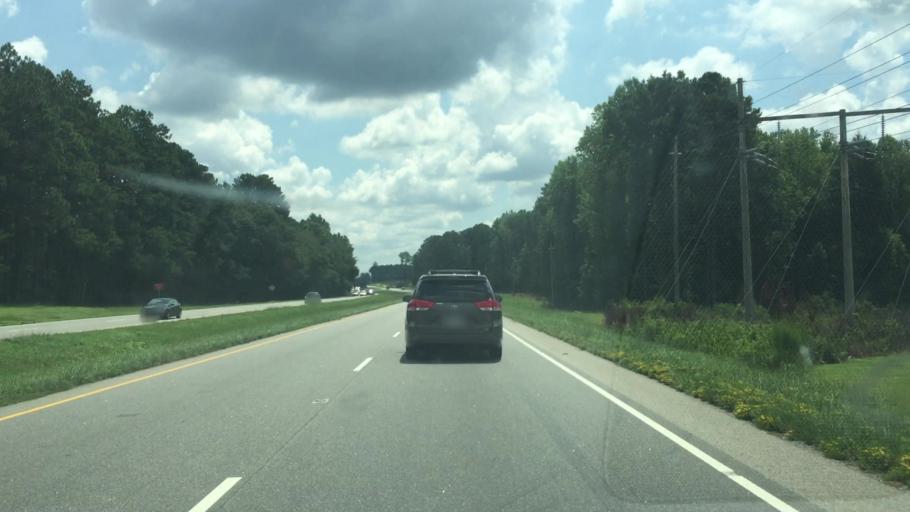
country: US
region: North Carolina
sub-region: Scotland County
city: Laurel Hill
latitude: 34.8147
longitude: -79.5670
